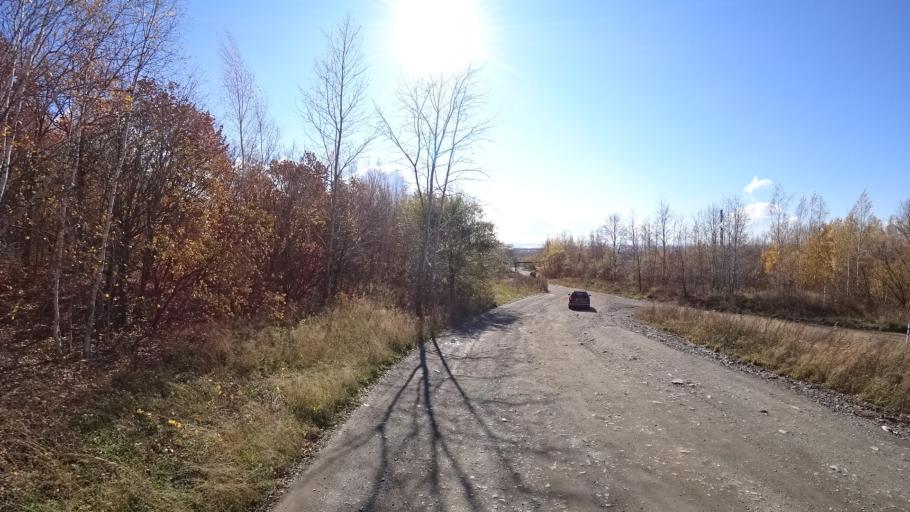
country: RU
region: Khabarovsk Krai
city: Amursk
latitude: 50.2403
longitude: 136.9019
